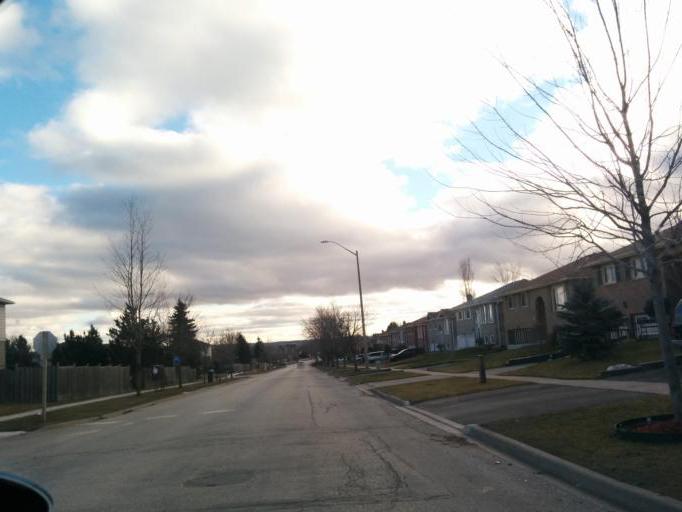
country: CA
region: Ontario
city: Bradford West Gwillimbury
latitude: 44.1034
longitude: -79.5770
